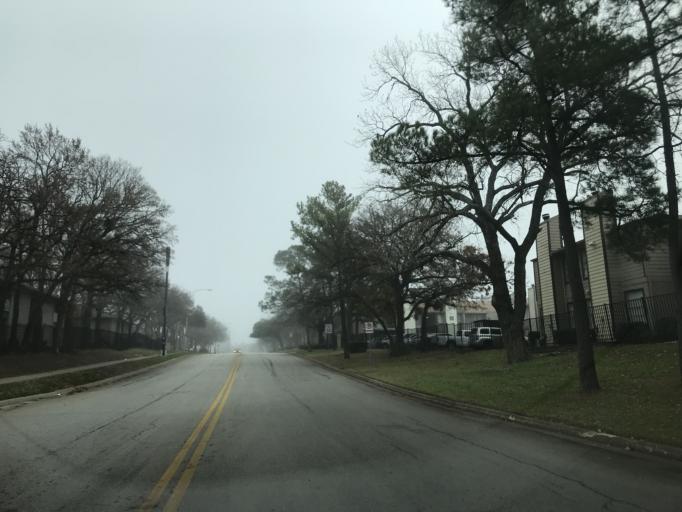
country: US
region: Texas
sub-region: Tarrant County
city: Arlington
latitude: 32.7697
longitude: -97.1050
